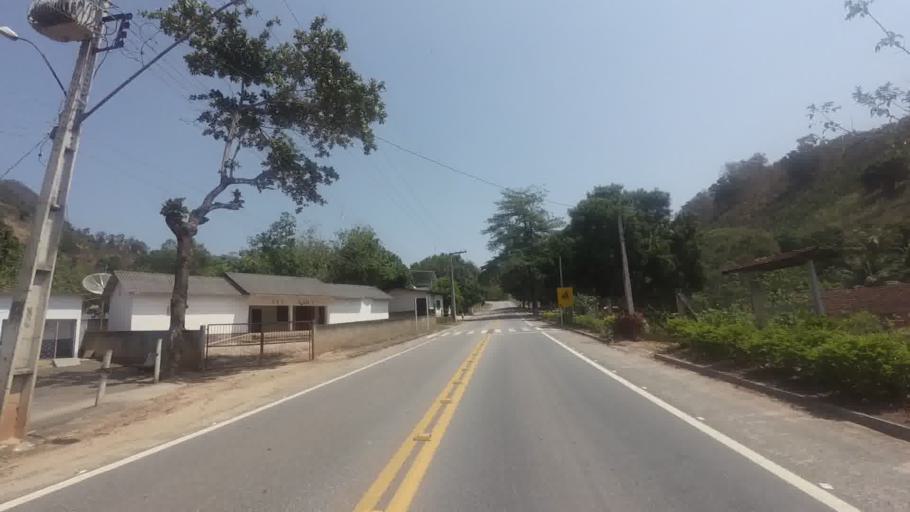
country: BR
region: Espirito Santo
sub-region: Cachoeiro De Itapemirim
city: Cachoeiro de Itapemirim
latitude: -20.8373
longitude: -41.2286
